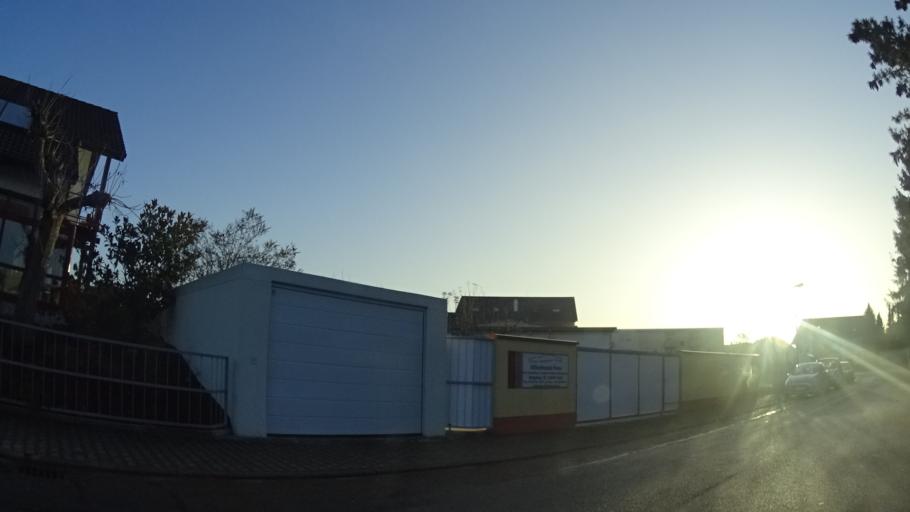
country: DE
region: Baden-Wuerttemberg
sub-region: Karlsruhe Region
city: Forst
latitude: 49.1548
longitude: 8.5790
